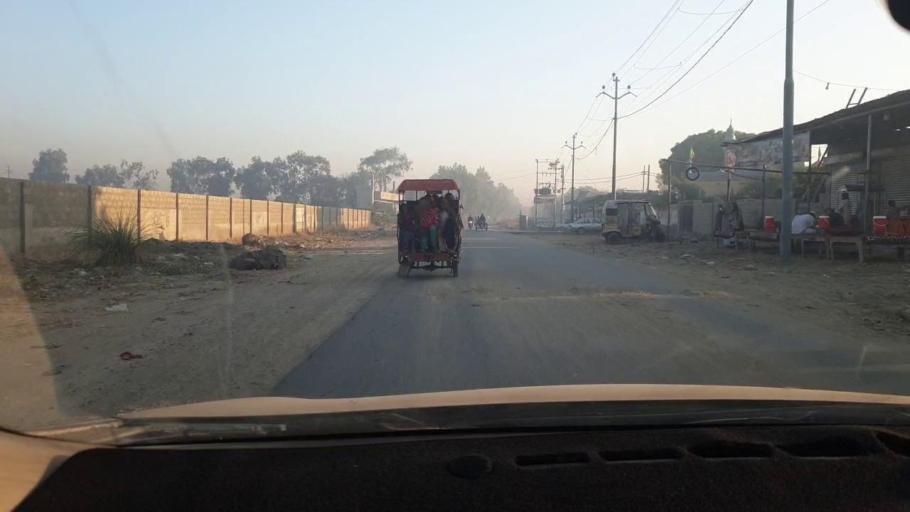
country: PK
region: Sindh
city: Malir Cantonment
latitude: 25.0049
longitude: 67.1532
